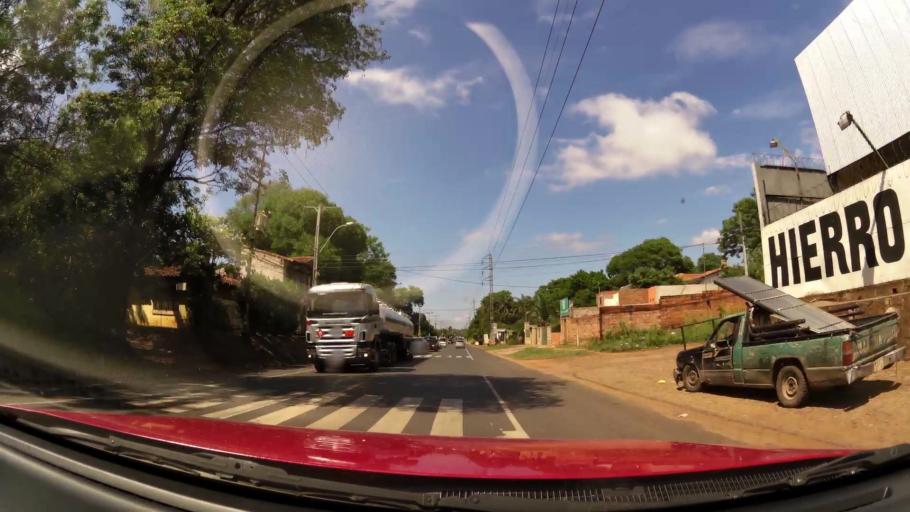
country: PY
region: Central
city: San Lorenzo
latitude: -25.3260
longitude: -57.5093
